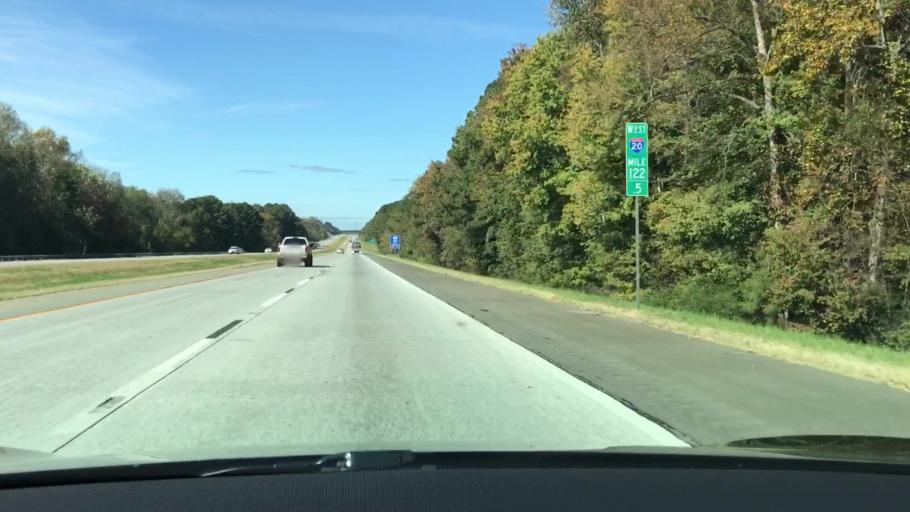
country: US
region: Georgia
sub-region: Putnam County
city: Jefferson
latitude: 33.5459
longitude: -83.3363
